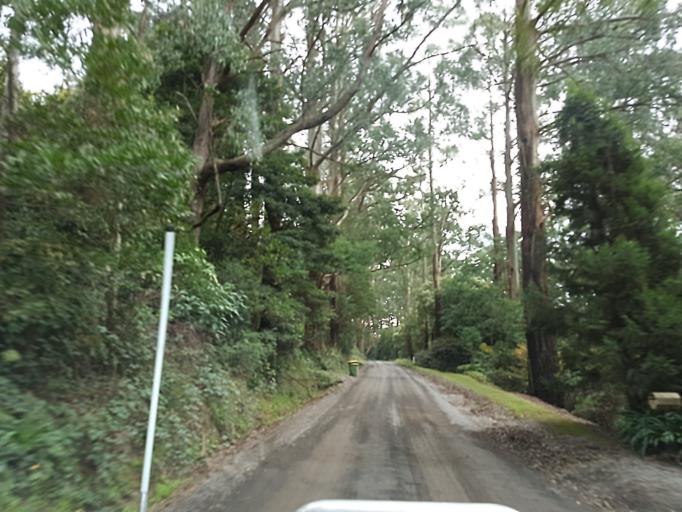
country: AU
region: Victoria
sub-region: Yarra Ranges
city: Monbulk
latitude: -37.8717
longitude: 145.3871
